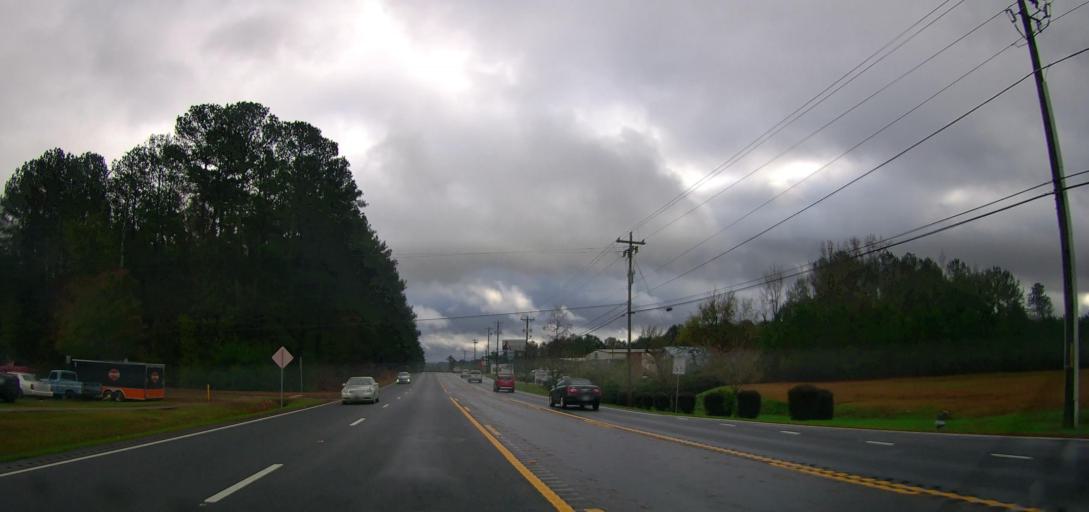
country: US
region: Georgia
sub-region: Clarke County
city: Country Club Estates
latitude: 34.0010
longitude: -83.3844
